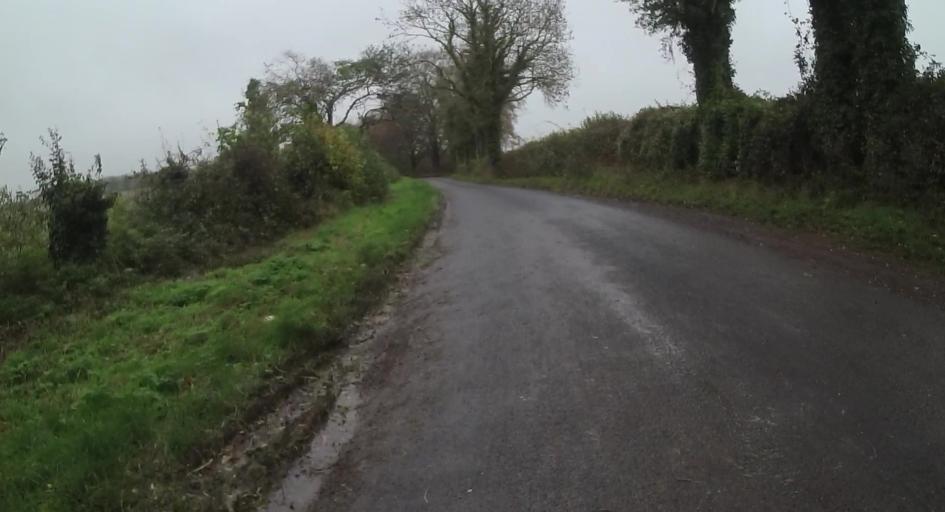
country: GB
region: England
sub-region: Hampshire
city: Four Marks
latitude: 51.1524
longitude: -1.1176
